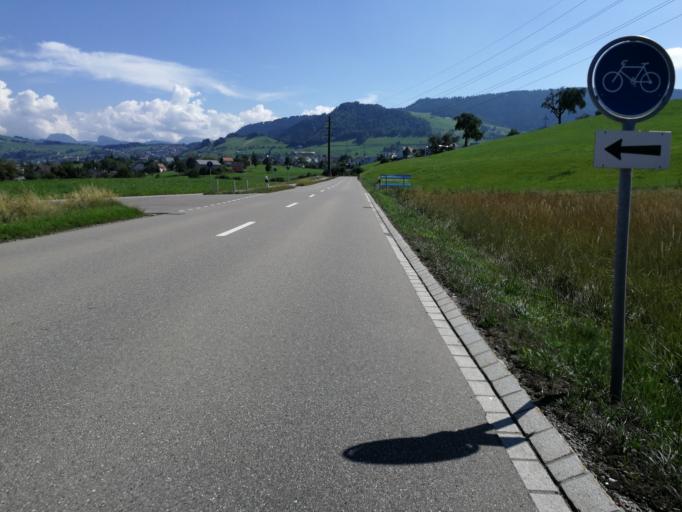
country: CH
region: Zurich
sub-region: Bezirk Horgen
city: Waedenswil / Eichweid
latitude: 47.1998
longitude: 8.6723
